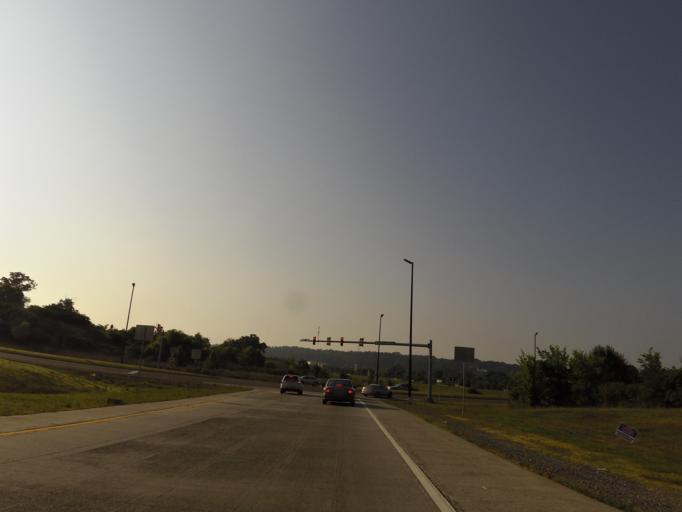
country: US
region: Tennessee
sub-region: Blount County
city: Eagleton Village
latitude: 35.8055
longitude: -83.9415
